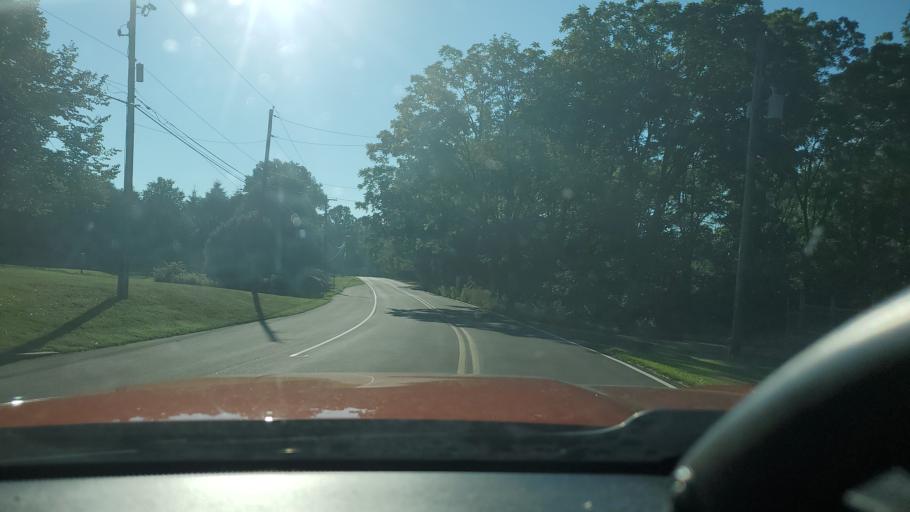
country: US
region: Pennsylvania
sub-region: Montgomery County
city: Harleysville
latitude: 40.2983
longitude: -75.3899
